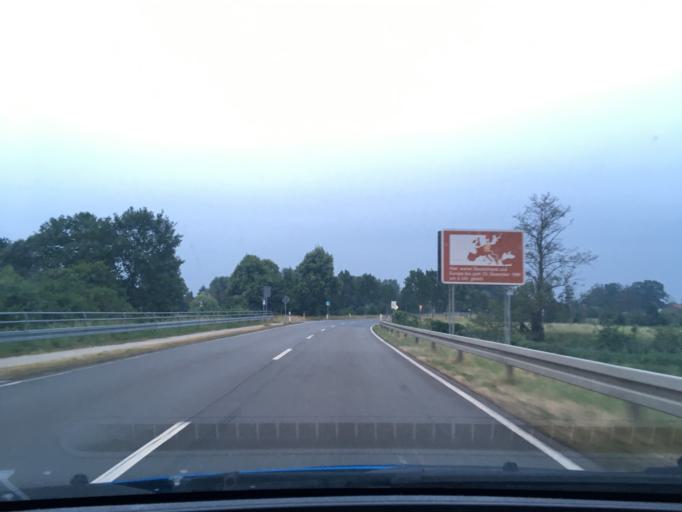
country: DE
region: Lower Saxony
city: Lubbow
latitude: 52.9012
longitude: 11.1794
